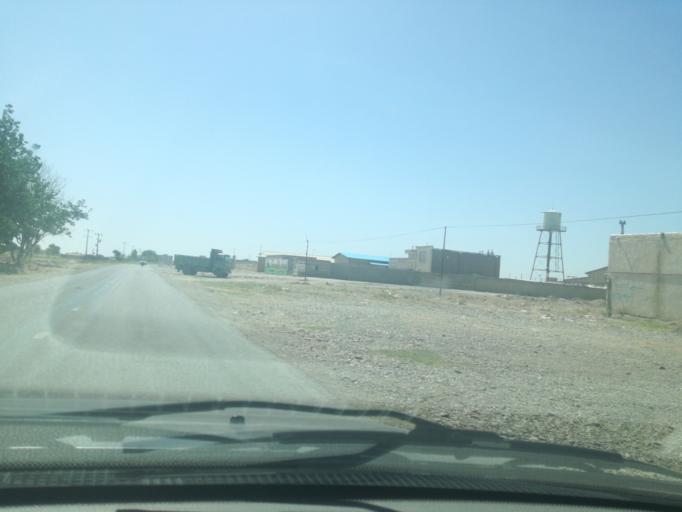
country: IR
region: Razavi Khorasan
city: Sarakhs
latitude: 36.5635
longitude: 61.1454
